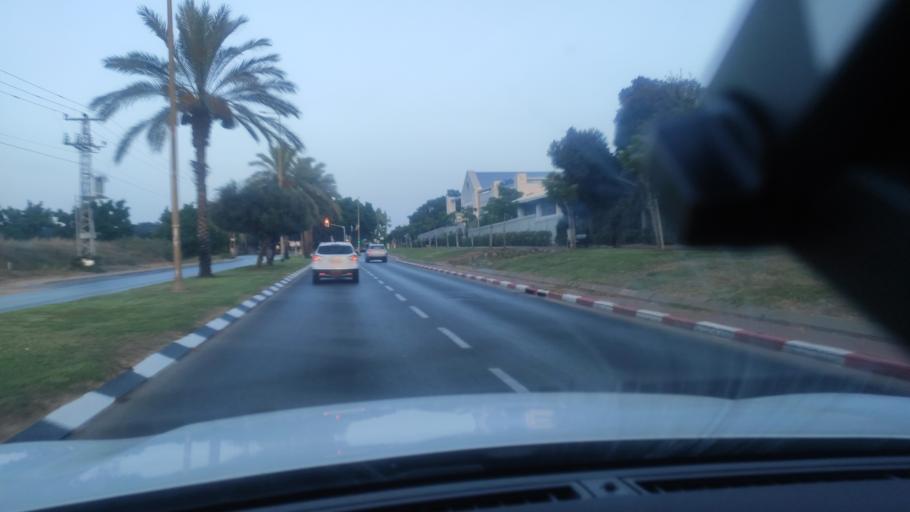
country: IL
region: Central District
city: Kfar Saba
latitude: 32.1838
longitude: 34.9185
